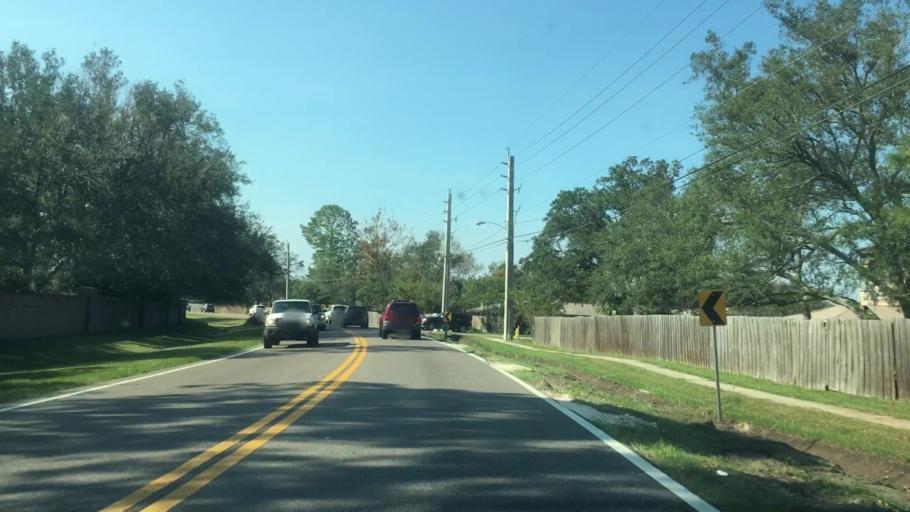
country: US
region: Florida
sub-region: Duval County
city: Neptune Beach
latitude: 30.2989
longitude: -81.4382
